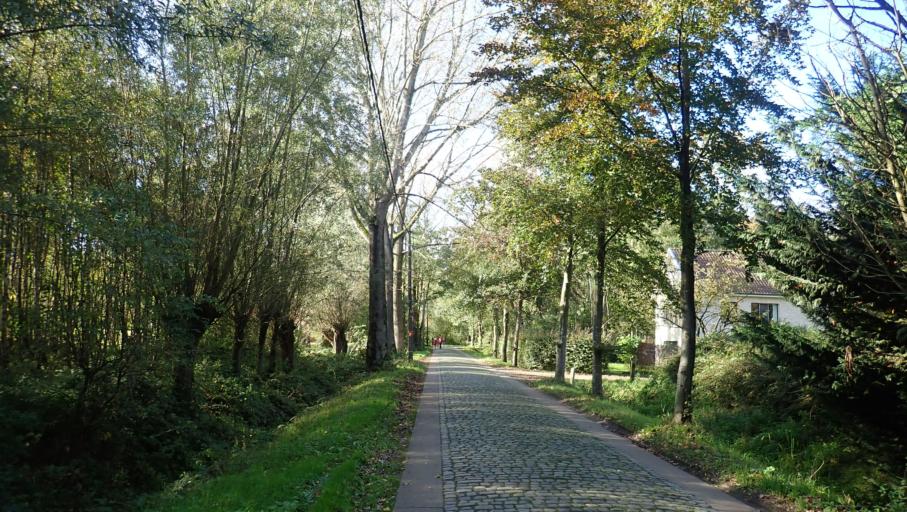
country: BE
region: Flanders
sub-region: Provincie Oost-Vlaanderen
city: Stekene
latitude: 51.1688
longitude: 4.0102
